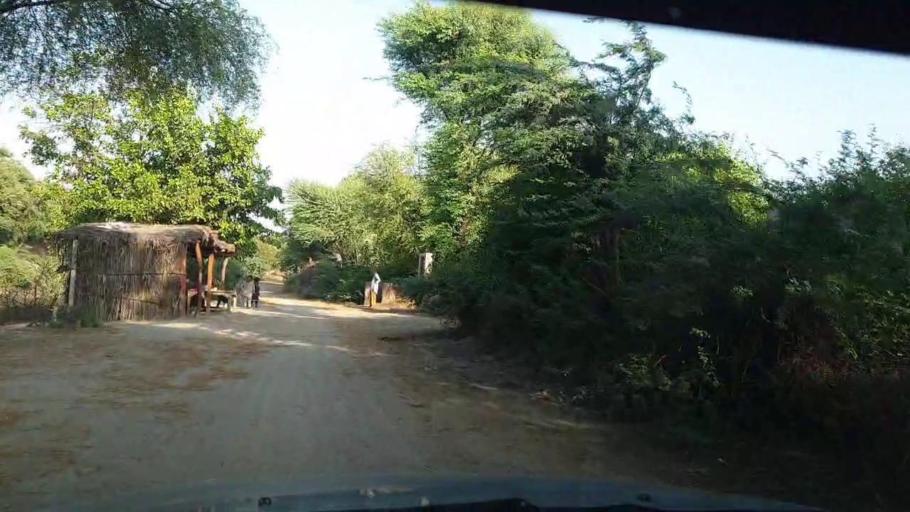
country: PK
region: Sindh
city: Matli
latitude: 25.0114
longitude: 68.7506
